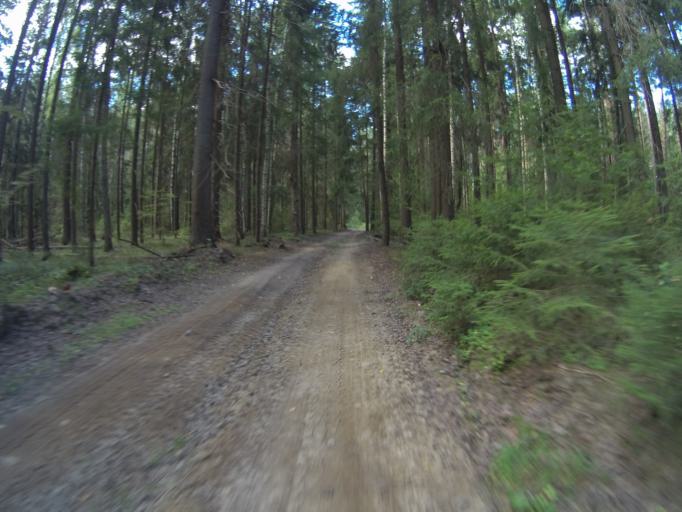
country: RU
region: Vladimir
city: Raduzhnyy
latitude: 55.8984
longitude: 40.1922
